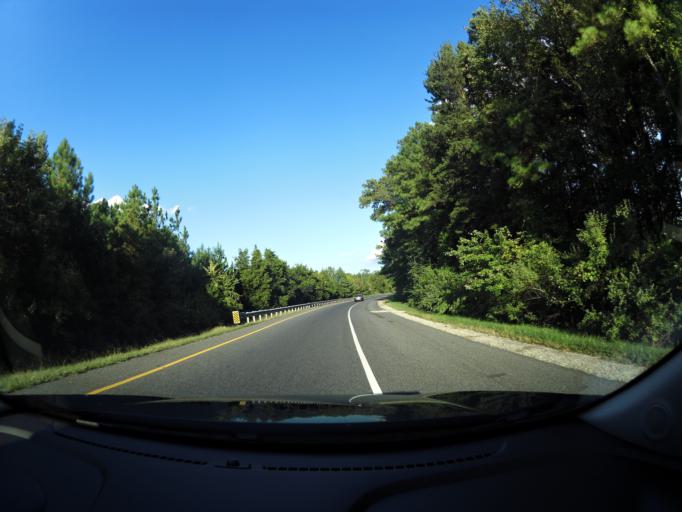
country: US
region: Maryland
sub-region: Howard County
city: West Elkridge
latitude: 39.1944
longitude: -76.7688
